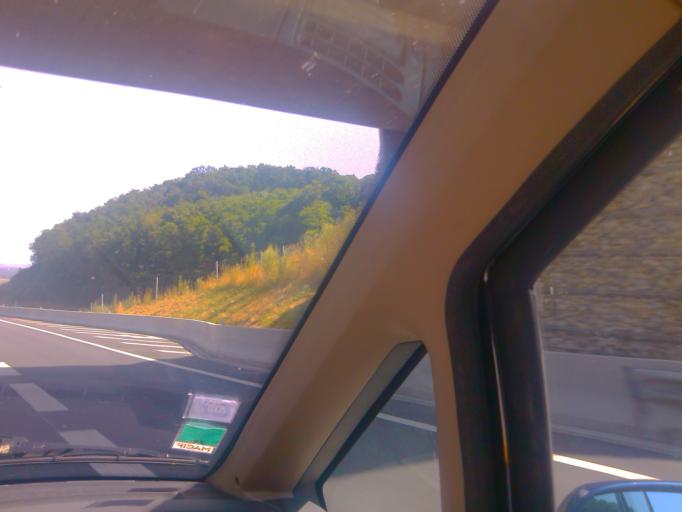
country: FR
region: Rhone-Alpes
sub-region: Departement de l'Ain
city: Beynost
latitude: 45.8507
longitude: 5.0077
